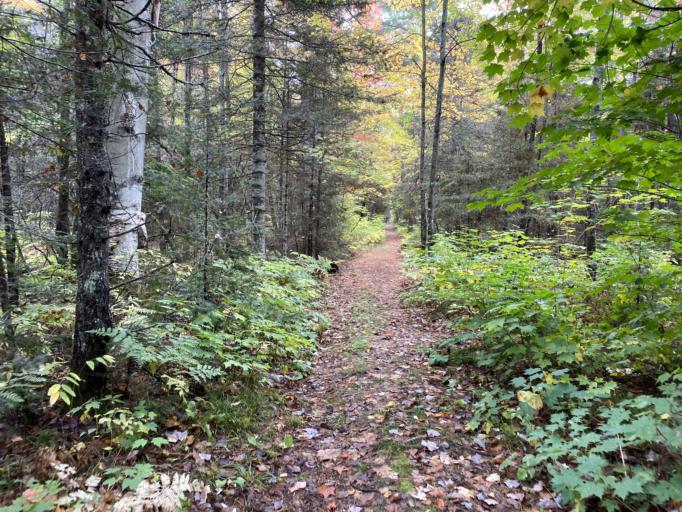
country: US
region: Michigan
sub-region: Marquette County
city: West Ishpeming
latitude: 46.5351
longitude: -87.9997
